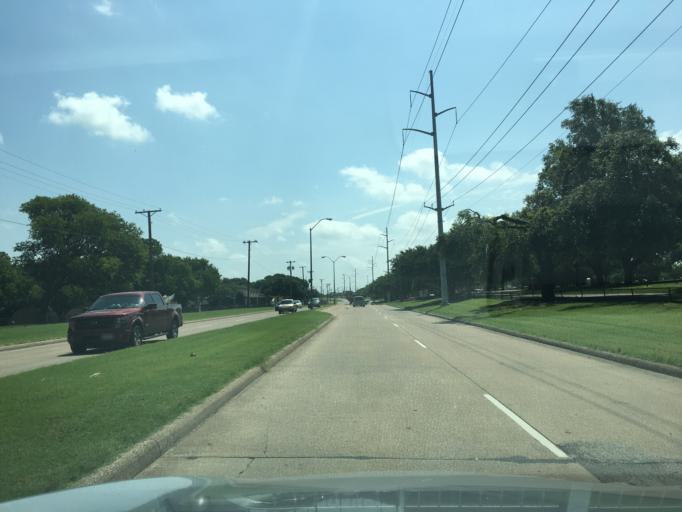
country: US
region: Texas
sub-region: Dallas County
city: Richardson
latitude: 32.9231
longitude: -96.7442
